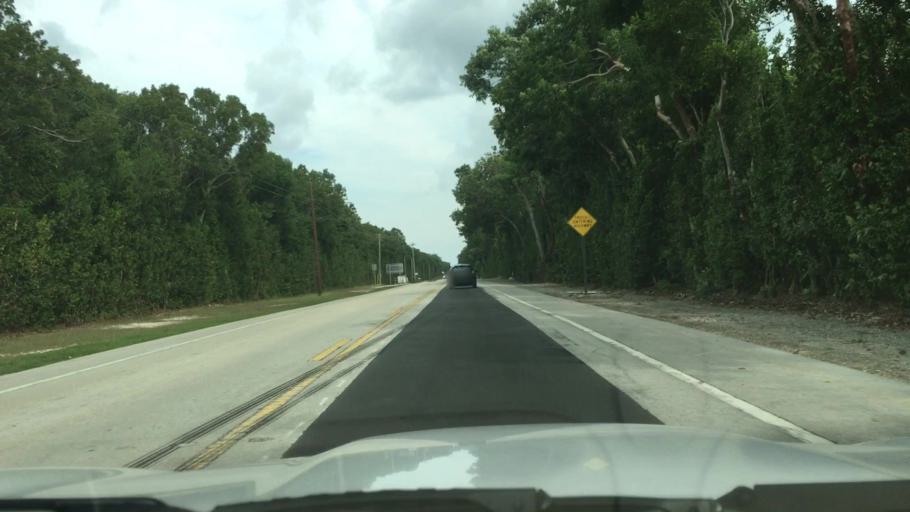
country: US
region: Florida
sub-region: Monroe County
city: North Key Largo
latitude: 25.2345
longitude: -80.3253
